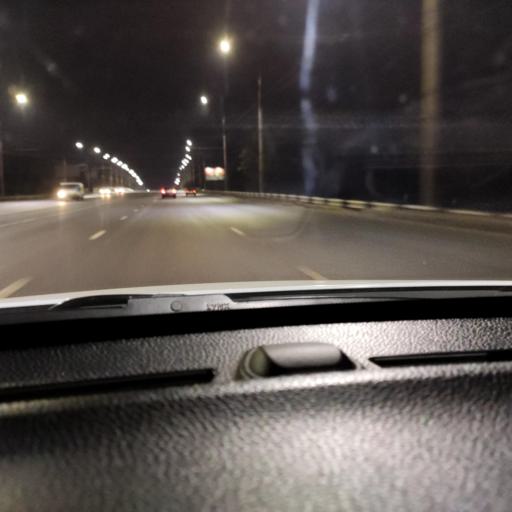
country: RU
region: Voronezj
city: Voronezh
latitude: 51.6330
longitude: 39.2270
